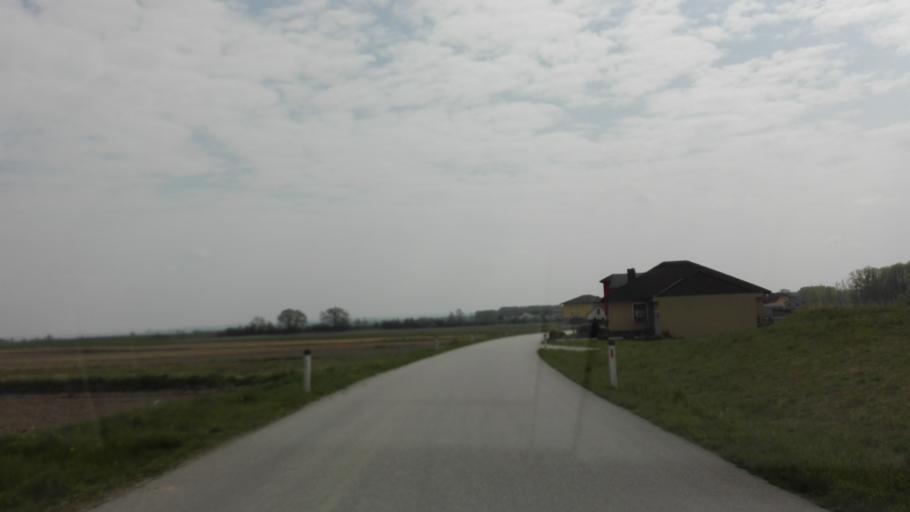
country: AT
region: Upper Austria
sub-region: Politischer Bezirk Perg
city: Perg
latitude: 48.2006
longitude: 14.6282
